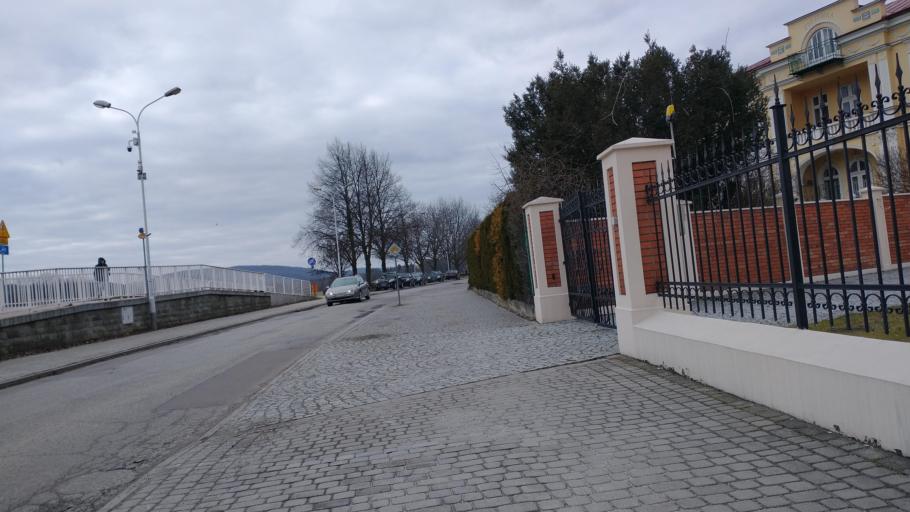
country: PL
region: Subcarpathian Voivodeship
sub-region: Przemysl
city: Przemysl
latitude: 49.7837
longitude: 22.7624
